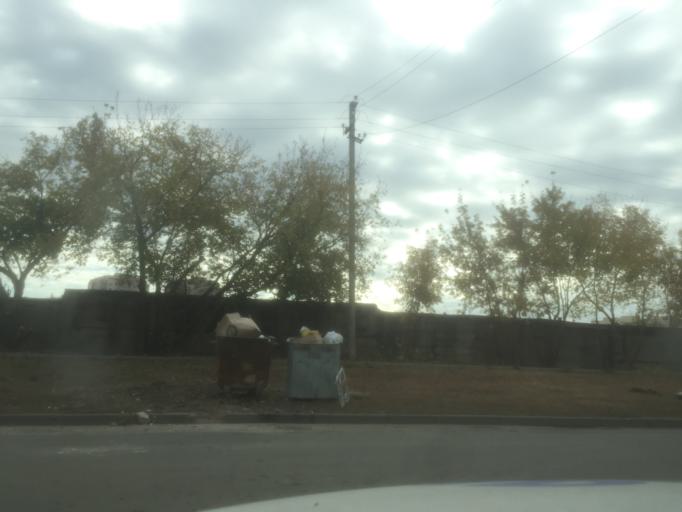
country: KZ
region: Astana Qalasy
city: Astana
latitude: 51.1736
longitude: 71.3738
